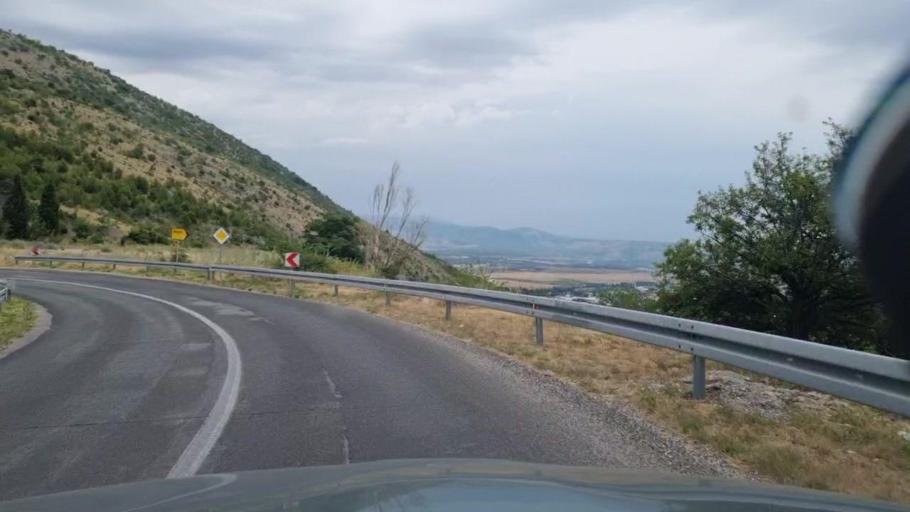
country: BA
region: Federation of Bosnia and Herzegovina
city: Rodoc
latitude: 43.3265
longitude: 17.7973
